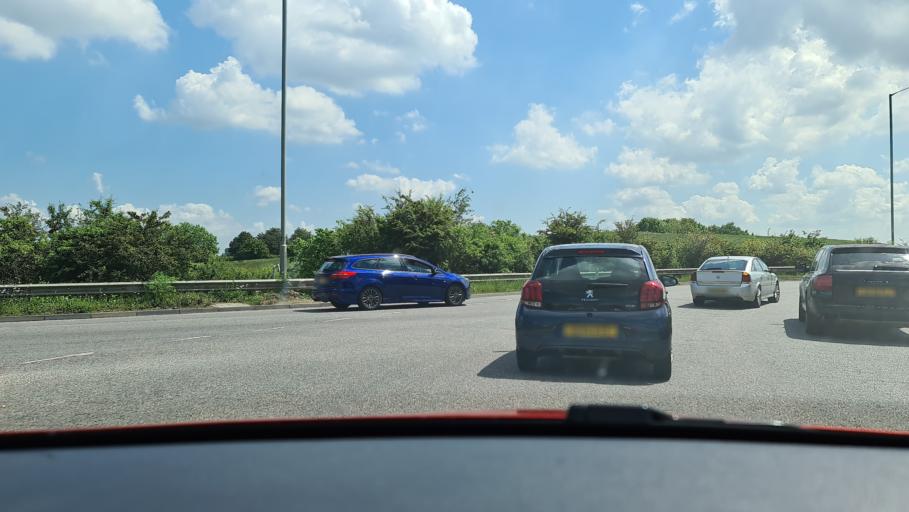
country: GB
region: England
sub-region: Milton Keynes
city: Broughton
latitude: 52.0596
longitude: -0.7003
